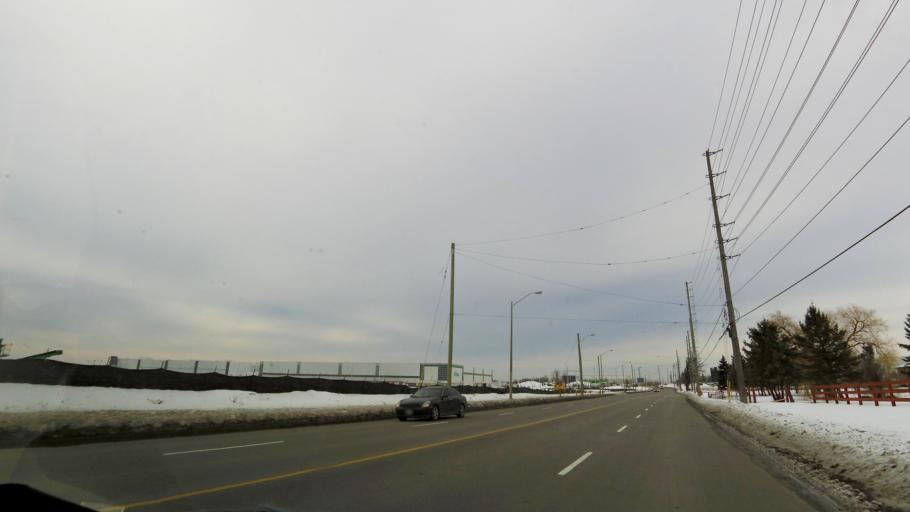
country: CA
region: Ontario
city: Brampton
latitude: 43.7851
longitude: -79.6507
